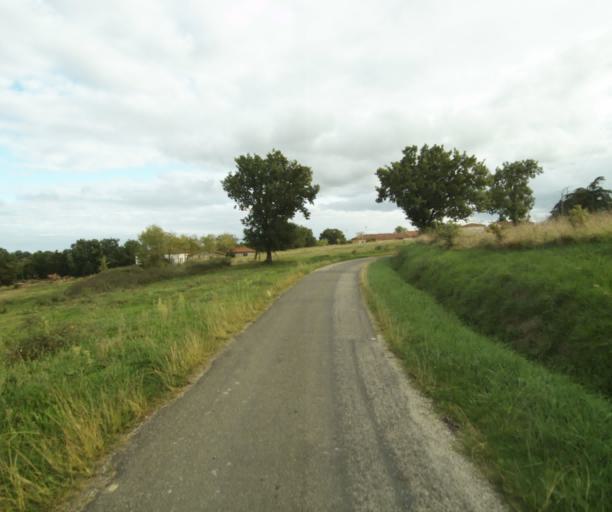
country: FR
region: Midi-Pyrenees
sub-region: Departement du Gers
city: Eauze
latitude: 43.9493
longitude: 0.0924
